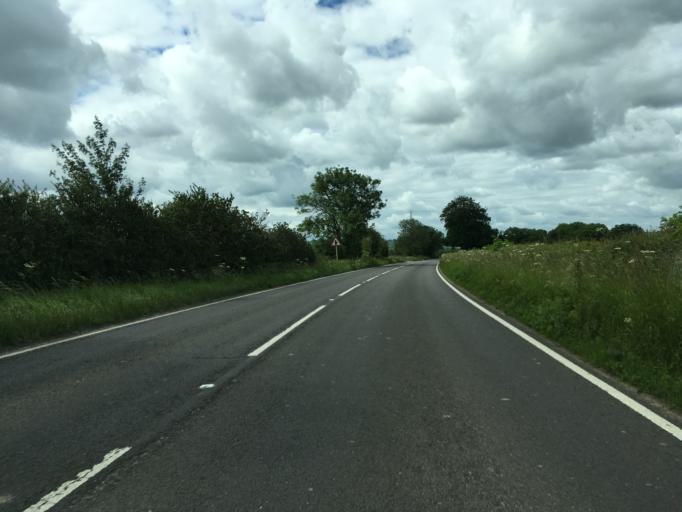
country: GB
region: England
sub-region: Oxfordshire
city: Shipton under Wychwood
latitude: 51.8743
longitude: -1.5806
